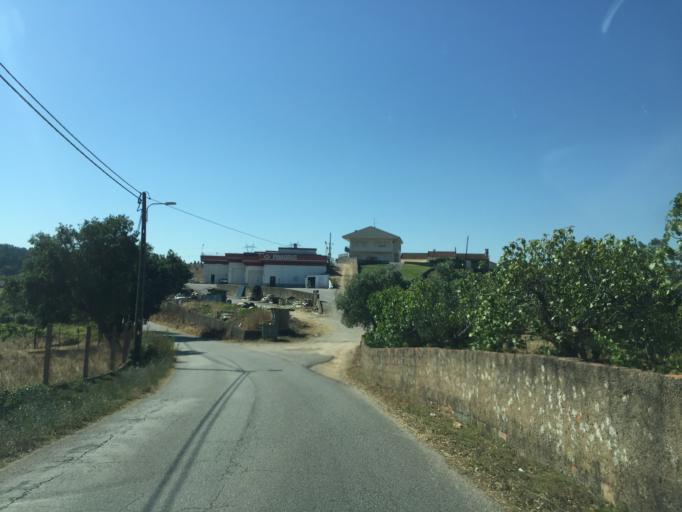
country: PT
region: Santarem
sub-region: Tomar
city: Tomar
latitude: 39.5739
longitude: -8.3261
